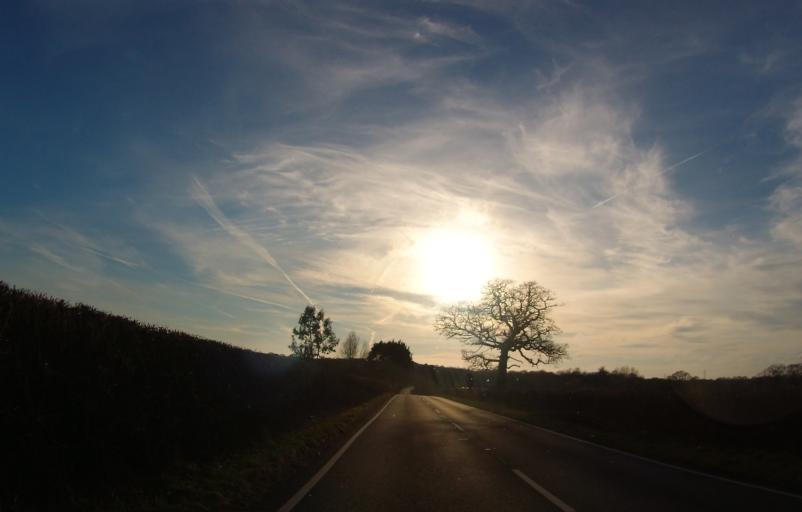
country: GB
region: England
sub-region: Isle of Wight
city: Newport
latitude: 50.7132
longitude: -1.2512
